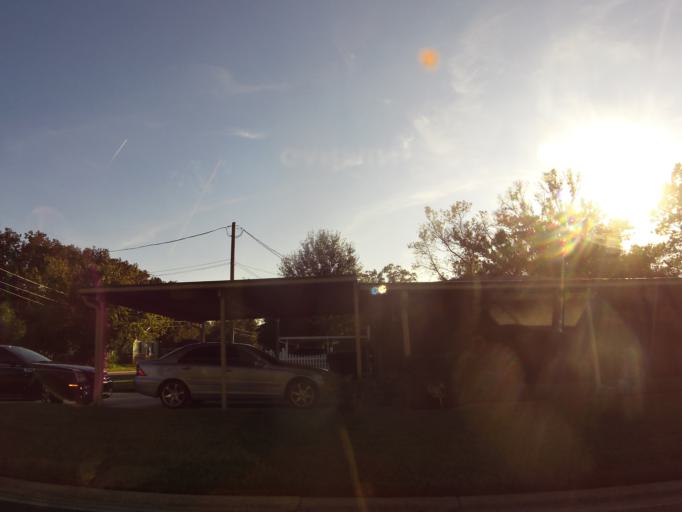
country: US
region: Florida
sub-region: Duval County
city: Jacksonville
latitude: 30.3549
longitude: -81.7061
